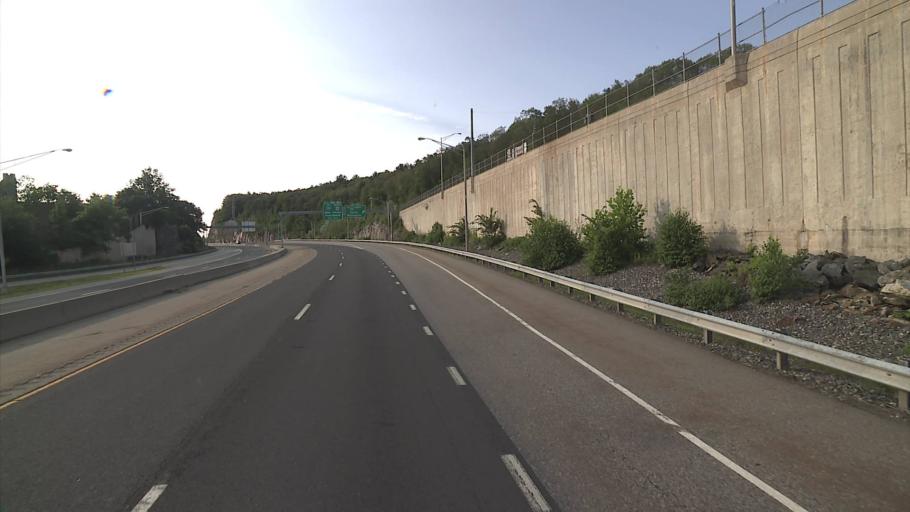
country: US
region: Connecticut
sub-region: New London County
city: Norwich
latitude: 41.5603
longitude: -72.1259
